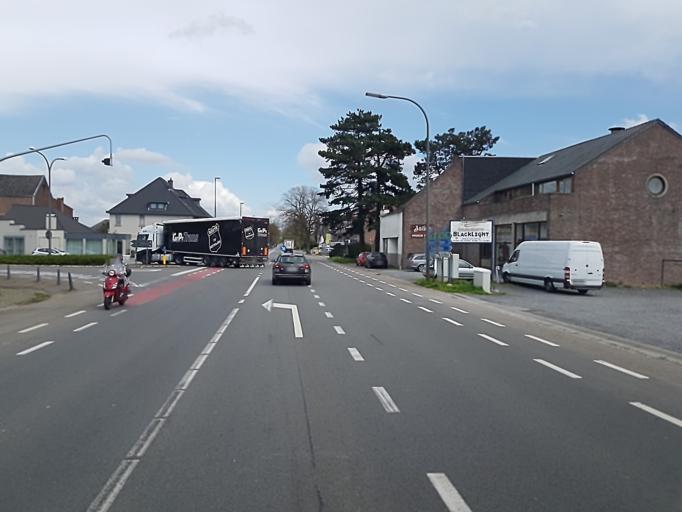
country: BE
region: Flanders
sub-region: Provincie Limburg
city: Riemst
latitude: 50.8241
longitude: 5.6254
